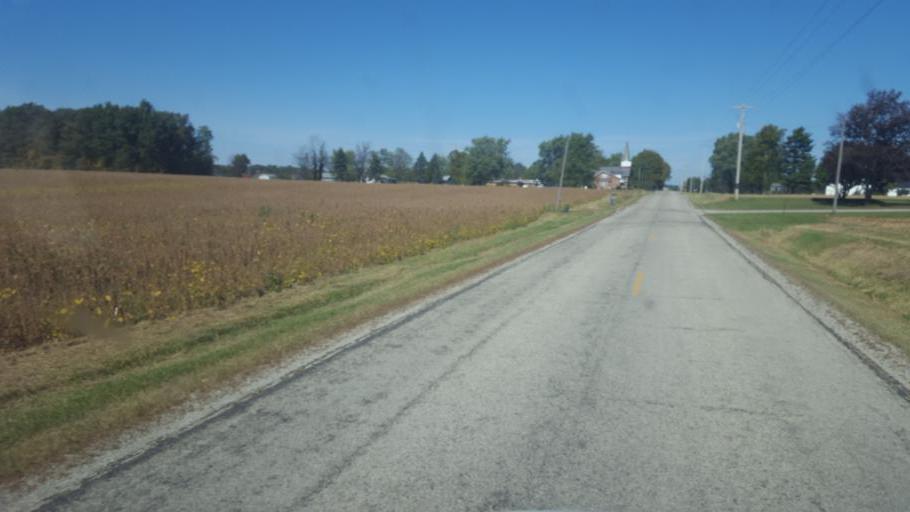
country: US
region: Ohio
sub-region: Huron County
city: Willard
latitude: 40.9648
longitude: -82.7910
